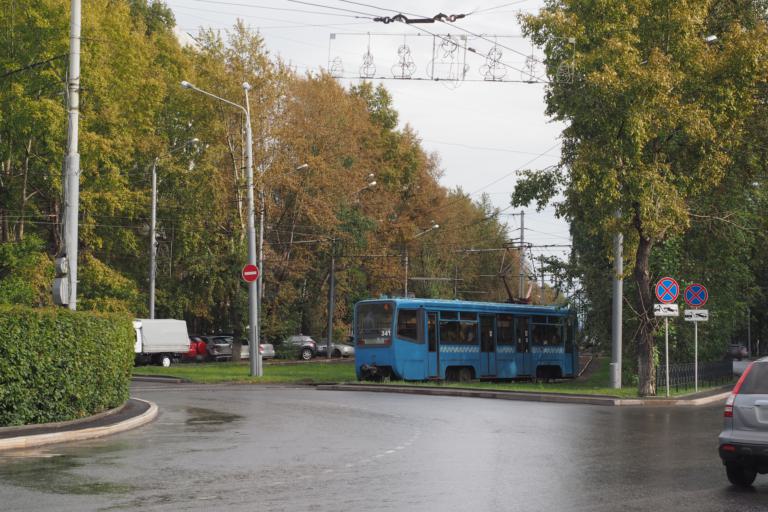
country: RU
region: Tomsk
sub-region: Tomskiy Rayon
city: Tomsk
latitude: 56.4662
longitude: 84.9811
